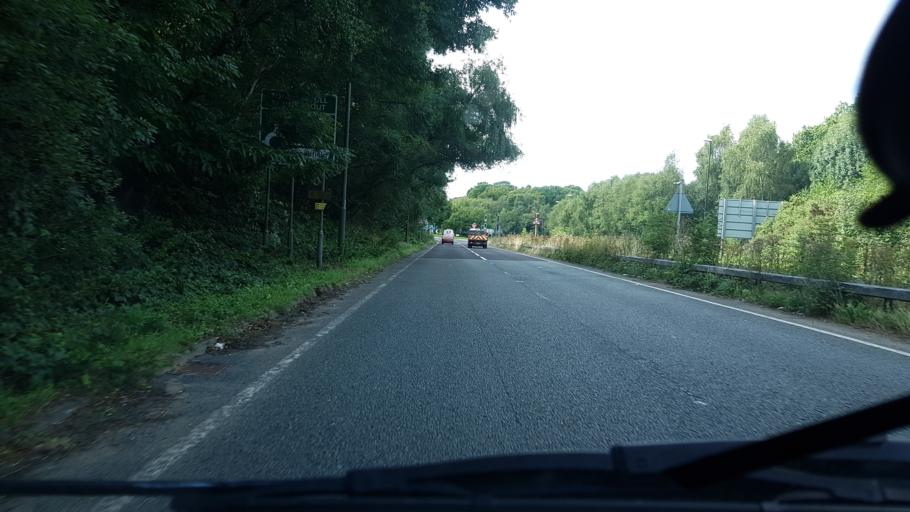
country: GB
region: England
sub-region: West Sussex
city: Broadfield
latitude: 51.0870
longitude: -0.1998
